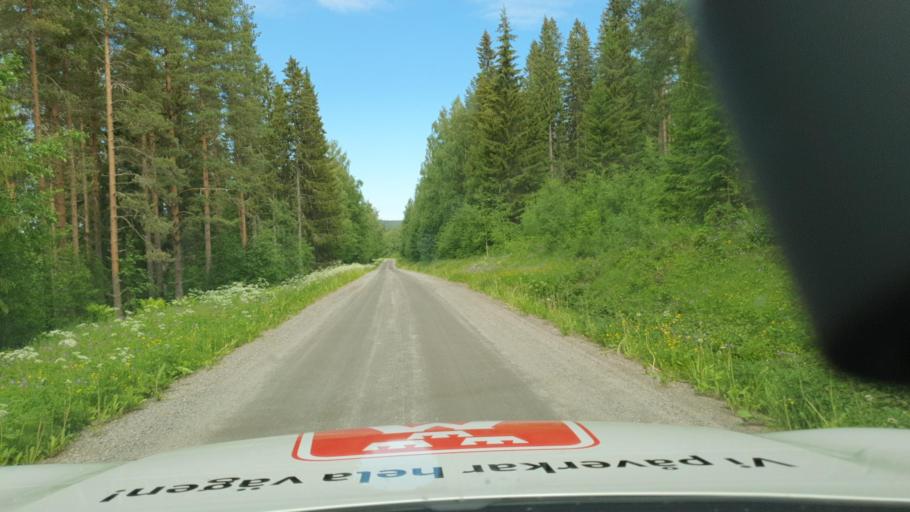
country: SE
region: Vaesterbotten
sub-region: Skelleftea Kommun
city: Forsbacka
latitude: 64.6719
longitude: 20.5312
